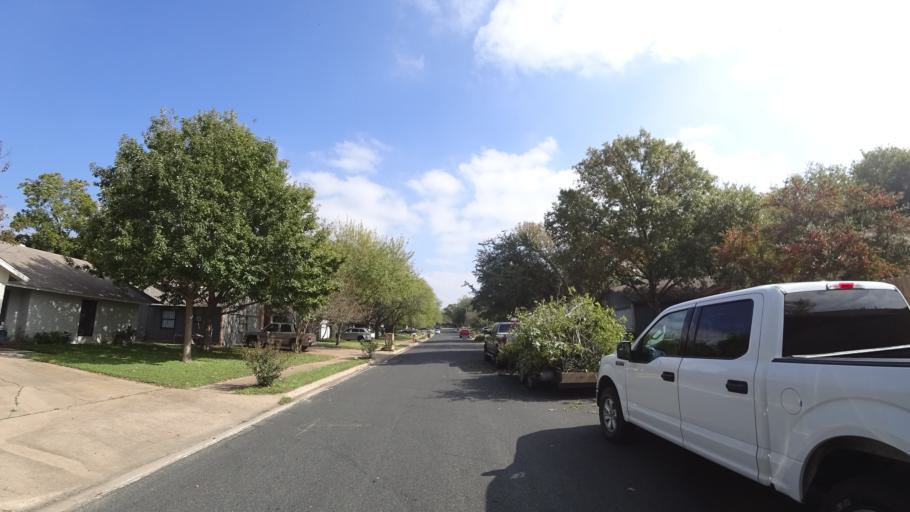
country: US
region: Texas
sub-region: Travis County
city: Shady Hollow
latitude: 30.2056
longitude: -97.8147
